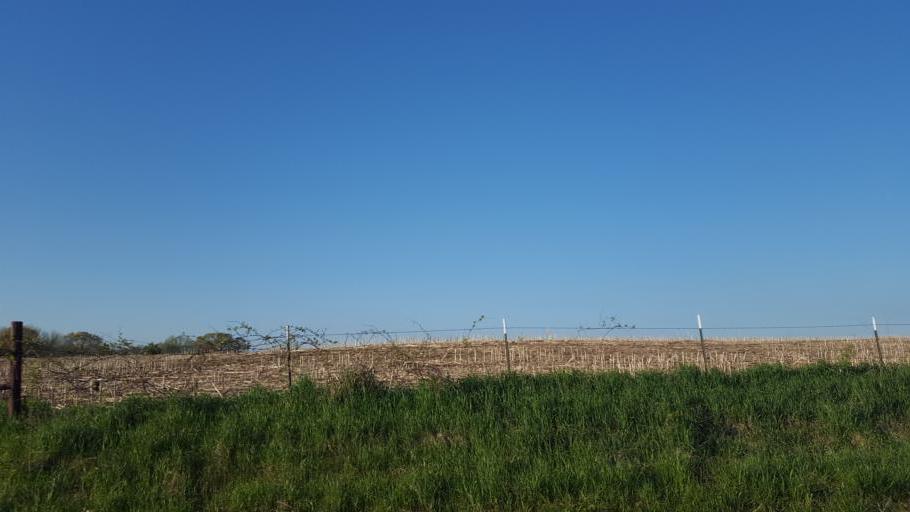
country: US
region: Wisconsin
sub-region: Vernon County
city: Hillsboro
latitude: 43.5737
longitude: -90.5453
